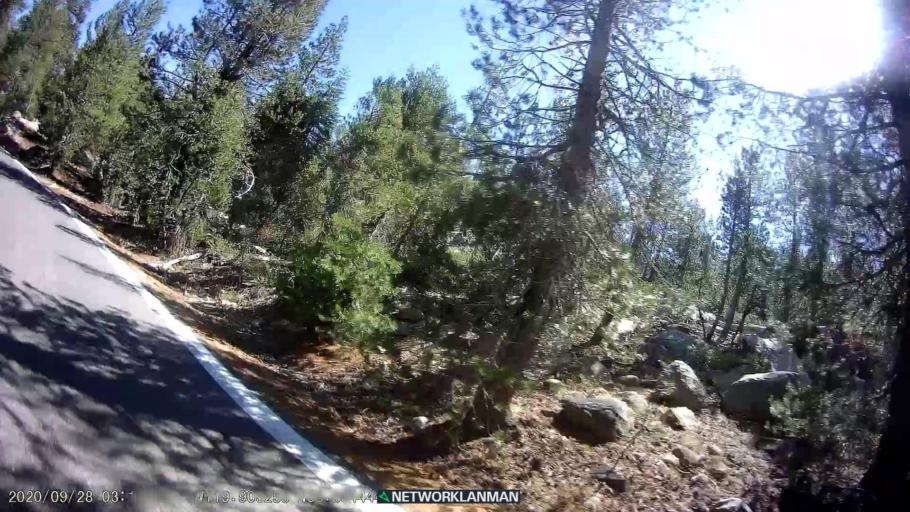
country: US
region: Nevada
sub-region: Douglas County
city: Gardnerville Ranchos
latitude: 38.5340
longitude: -119.9032
